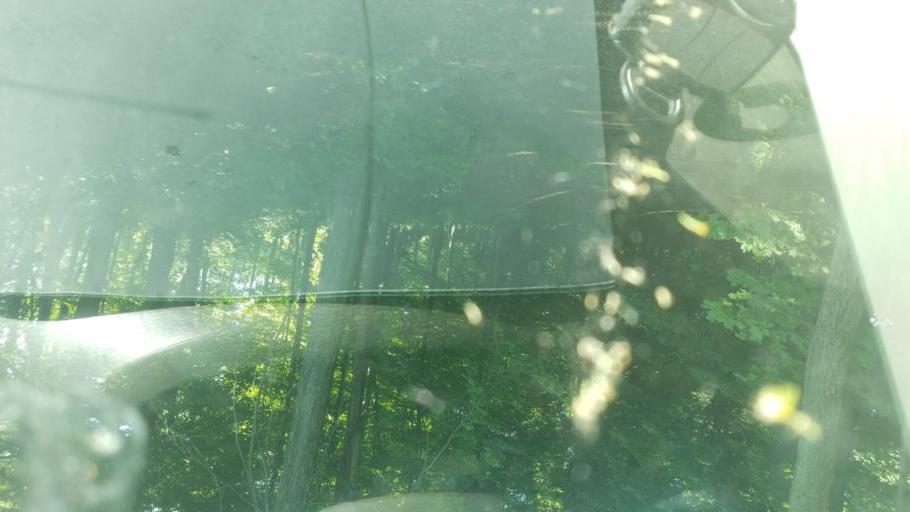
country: US
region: Ohio
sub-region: Sandusky County
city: Bellville
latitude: 40.6025
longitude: -82.5770
